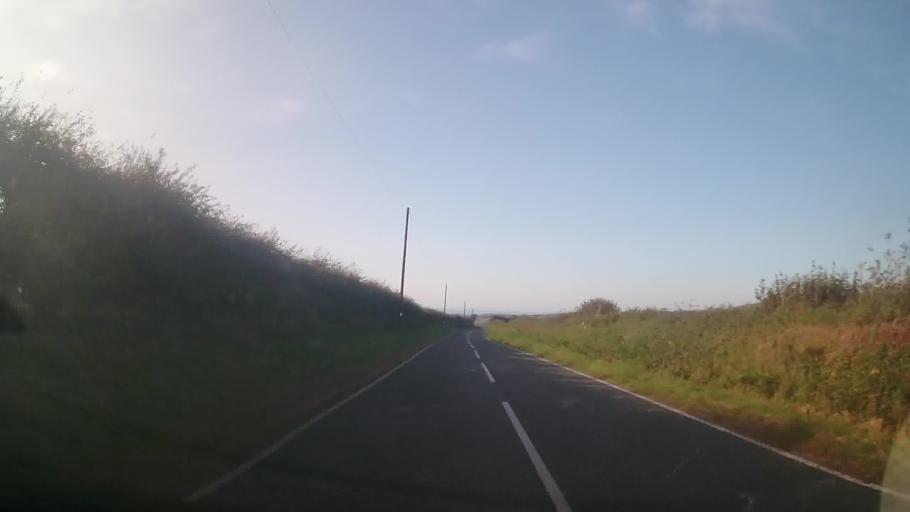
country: GB
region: Wales
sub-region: Pembrokeshire
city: Ambleston
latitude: 51.9669
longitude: -4.9027
